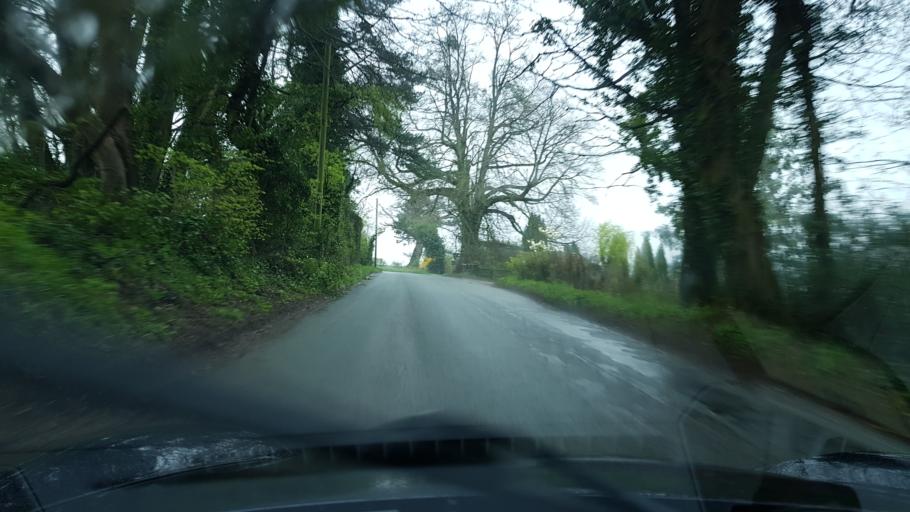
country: GB
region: England
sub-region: Herefordshire
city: Lea
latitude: 51.8865
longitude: -2.4839
